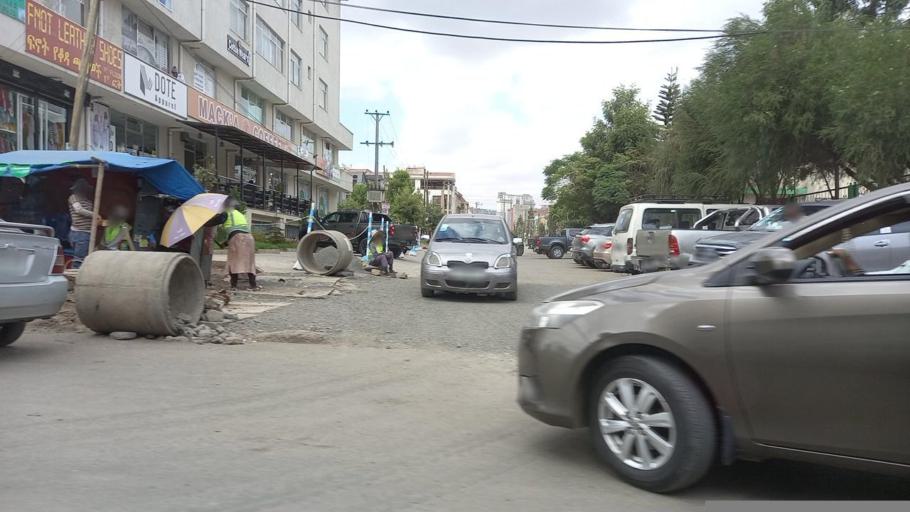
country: ET
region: Adis Abeba
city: Addis Ababa
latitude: 9.0101
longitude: 38.8508
